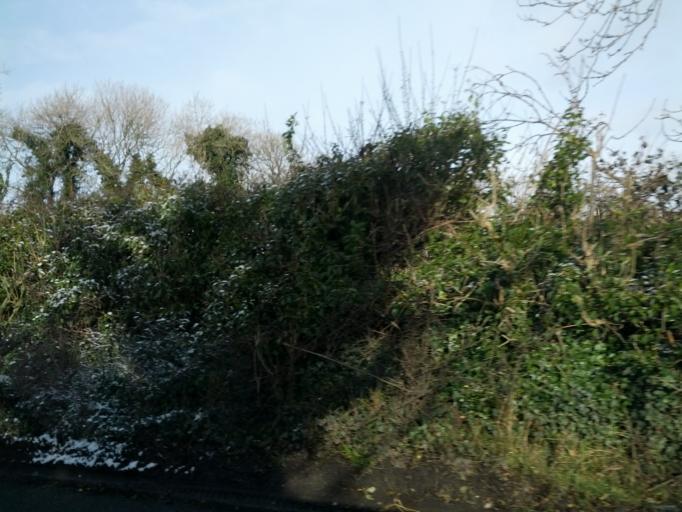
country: IE
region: Connaught
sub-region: County Galway
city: Gort
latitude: 53.1698
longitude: -8.7865
